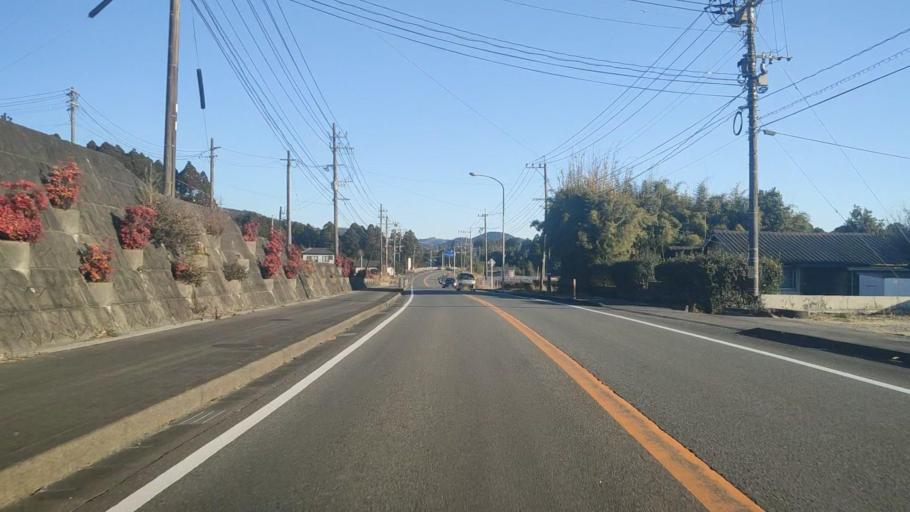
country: JP
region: Miyazaki
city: Takanabe
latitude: 32.3074
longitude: 131.5838
